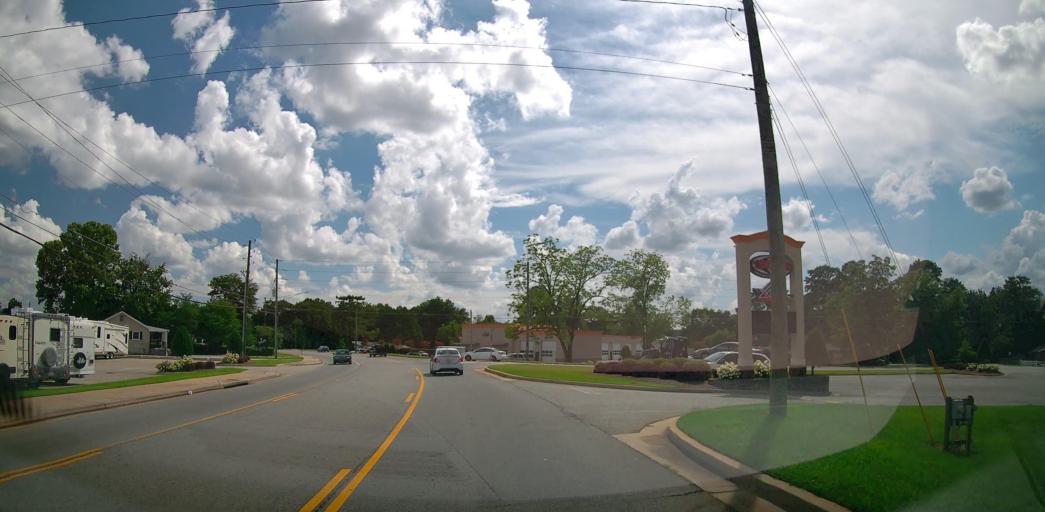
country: US
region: Georgia
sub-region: Houston County
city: Centerville
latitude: 32.6057
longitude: -83.6602
